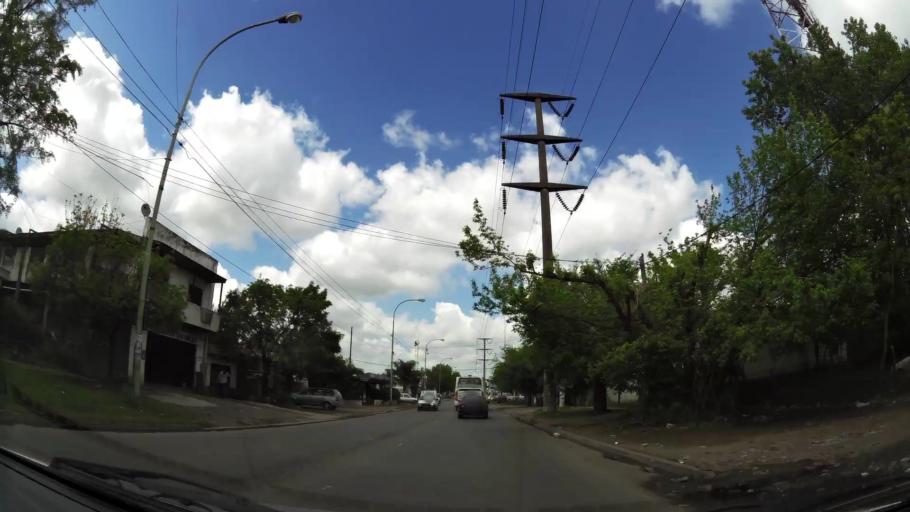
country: AR
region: Buenos Aires
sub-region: Partido de Quilmes
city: Quilmes
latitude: -34.8362
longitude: -58.1867
